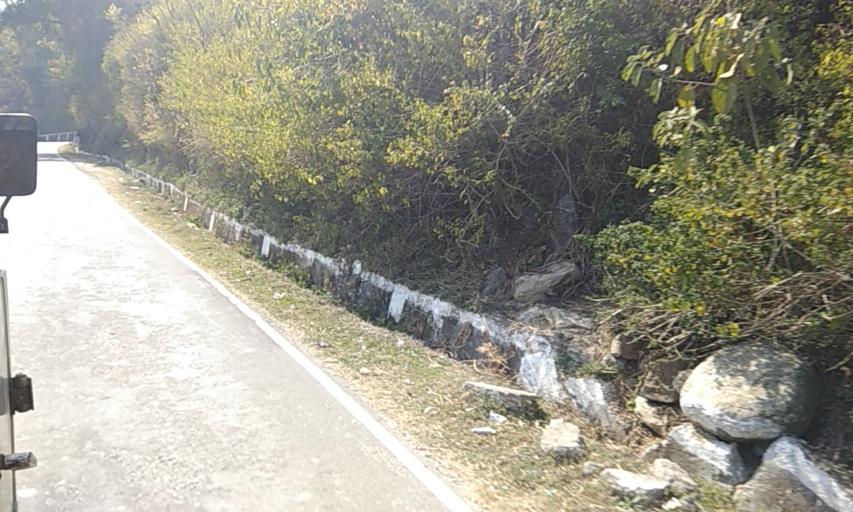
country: IN
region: Himachal Pradesh
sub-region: Kangra
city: Dharmsala
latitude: 32.1615
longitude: 76.4052
